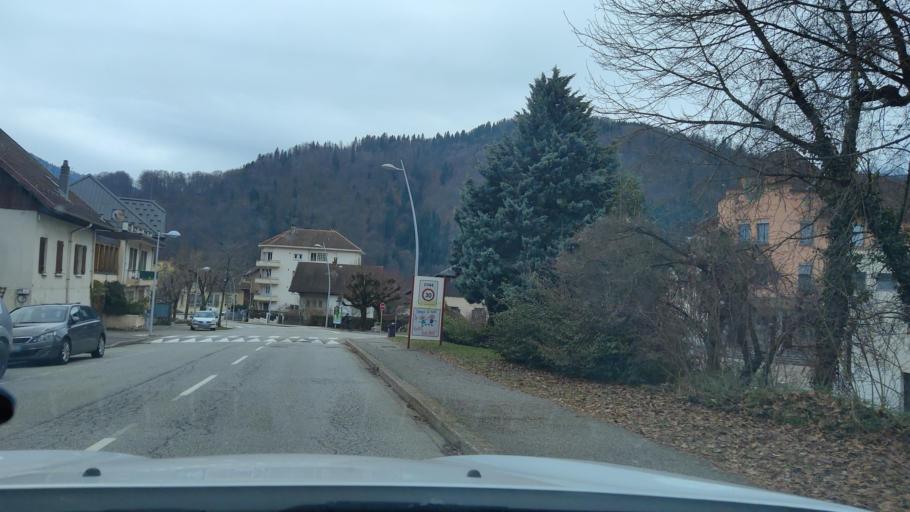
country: FR
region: Rhone-Alpes
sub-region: Departement de la Savoie
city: Ugine
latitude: 45.7515
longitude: 6.4174
